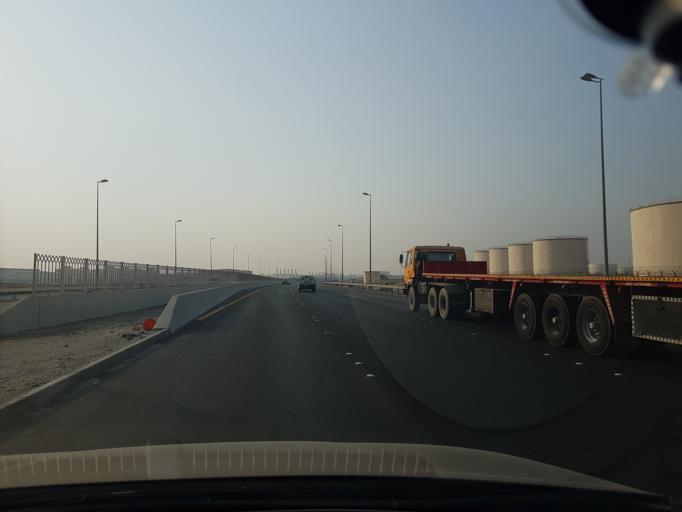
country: BH
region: Northern
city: Sitrah
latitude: 26.1001
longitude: 50.6045
